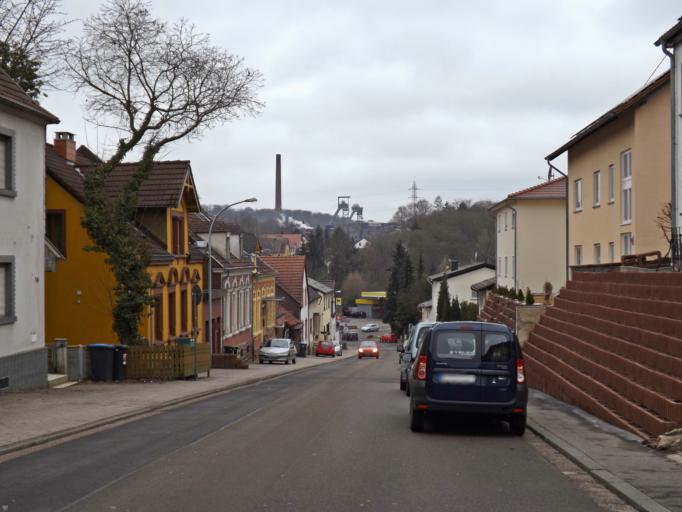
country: DE
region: Saarland
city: Schiffweiler
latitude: 49.3551
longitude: 7.1248
